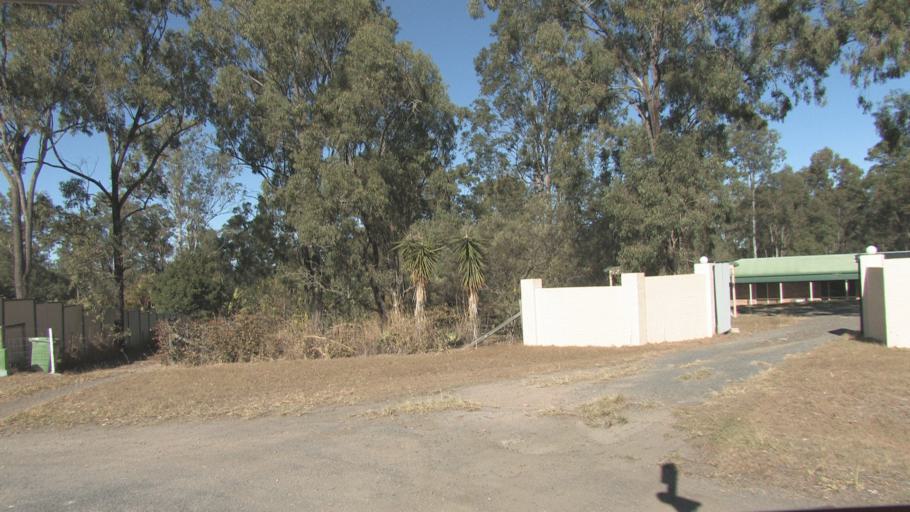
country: AU
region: Queensland
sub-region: Logan
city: North Maclean
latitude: -27.8288
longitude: 152.9374
